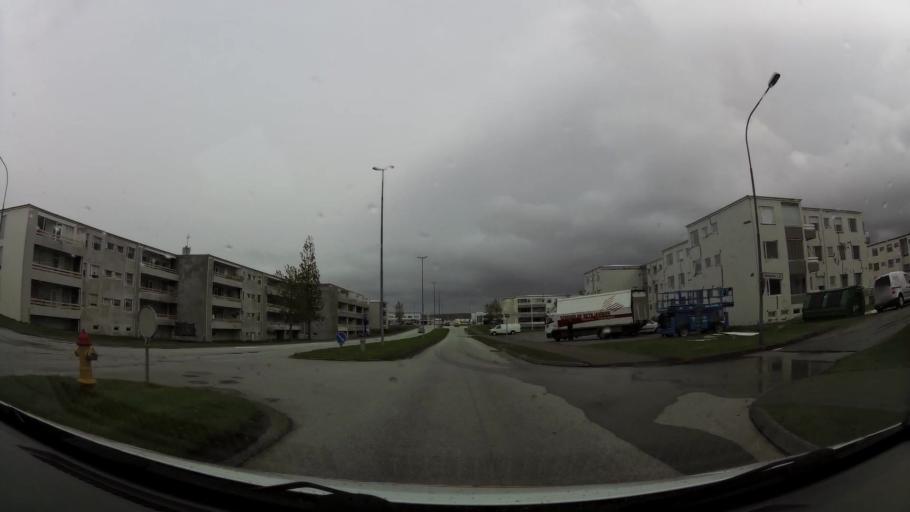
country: IS
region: Capital Region
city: Hafnarfjoerdur
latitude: 64.0790
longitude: -21.9547
